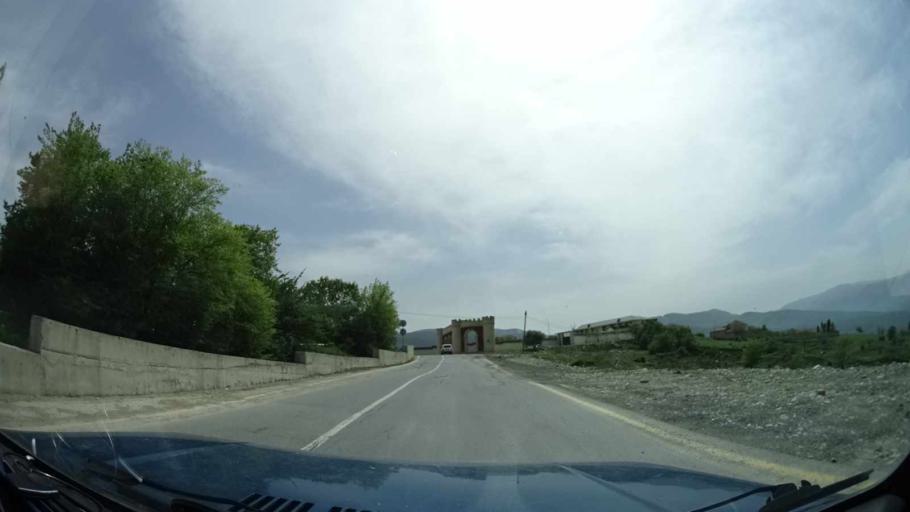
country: AZ
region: Xizi
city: Khyzy
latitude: 40.9145
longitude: 49.0709
